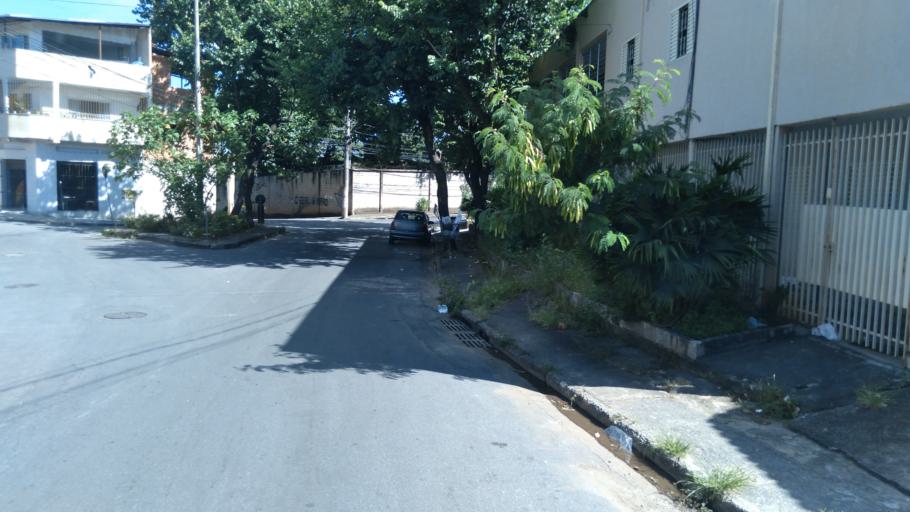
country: BR
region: Minas Gerais
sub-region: Belo Horizonte
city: Belo Horizonte
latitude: -19.8520
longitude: -43.9139
